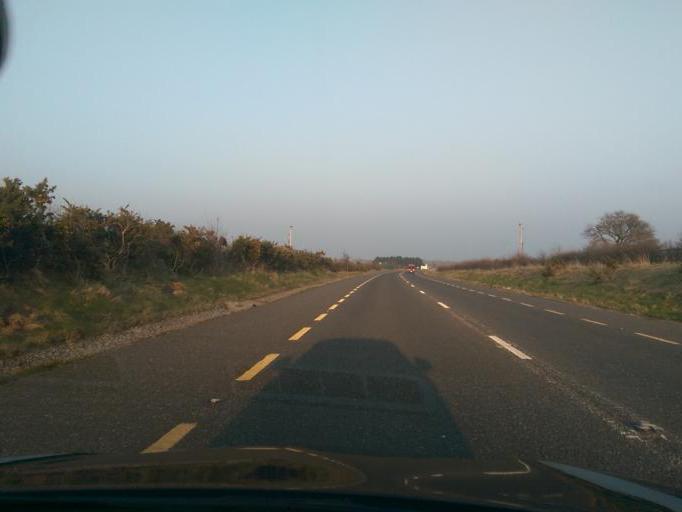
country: IE
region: Connaught
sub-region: County Galway
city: Loughrea
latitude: 53.2069
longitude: -8.5815
